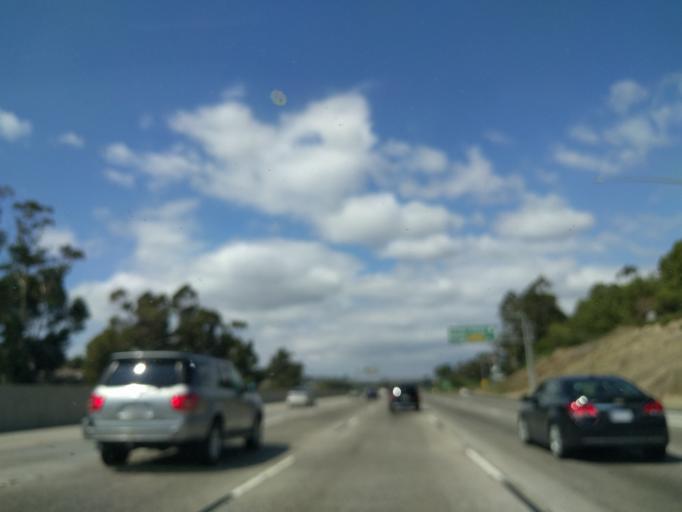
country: US
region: California
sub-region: Orange County
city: Ladera Ranch
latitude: 33.5549
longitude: -117.6728
